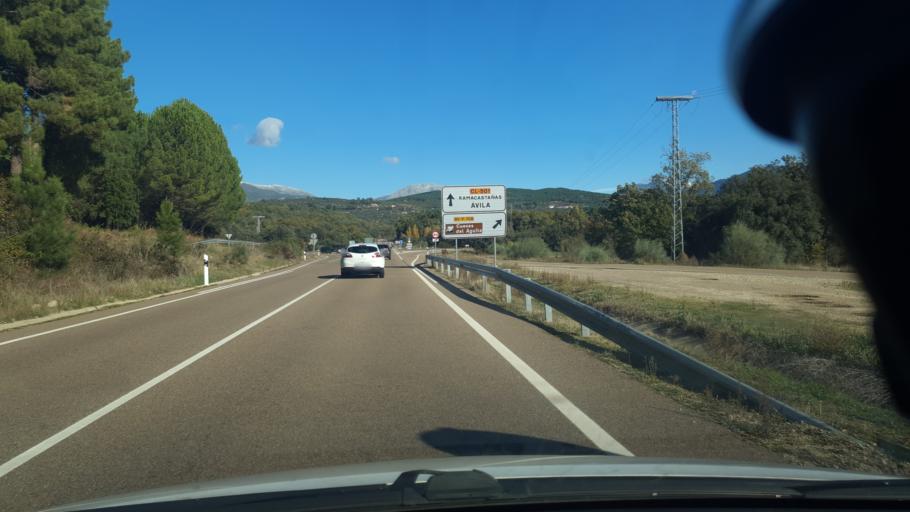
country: ES
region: Castille and Leon
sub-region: Provincia de Avila
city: Arenas de San Pedro
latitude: 40.1781
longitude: -5.0883
